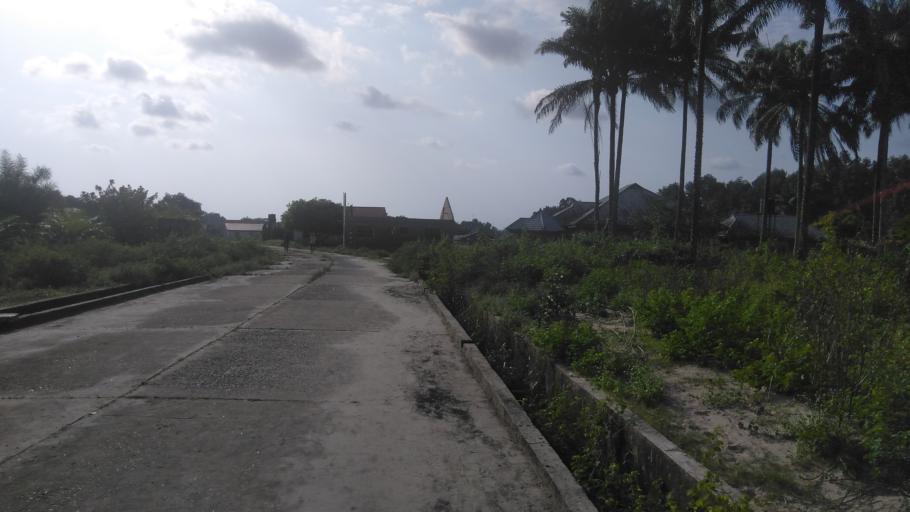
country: NG
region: Delta
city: Sapele
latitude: 5.8405
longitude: 5.1252
